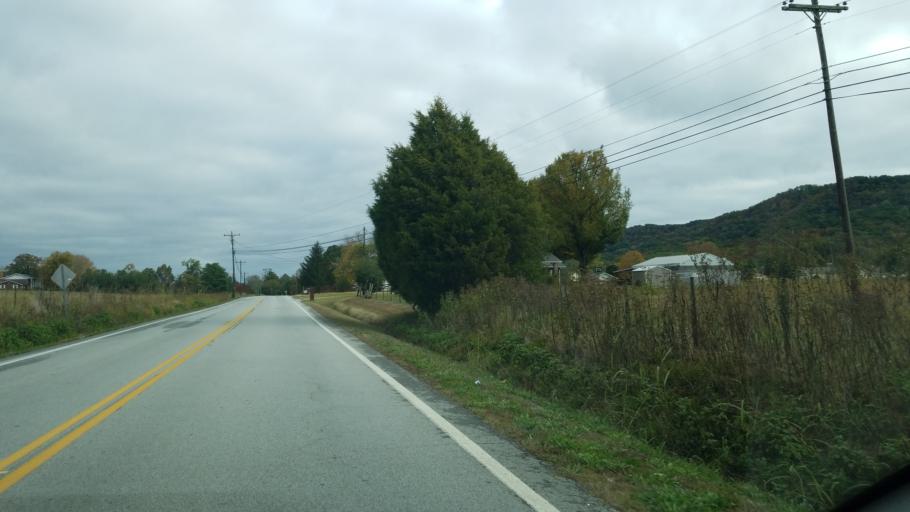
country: US
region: Tennessee
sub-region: Hamilton County
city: Lakesite
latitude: 35.1829
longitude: -85.0244
